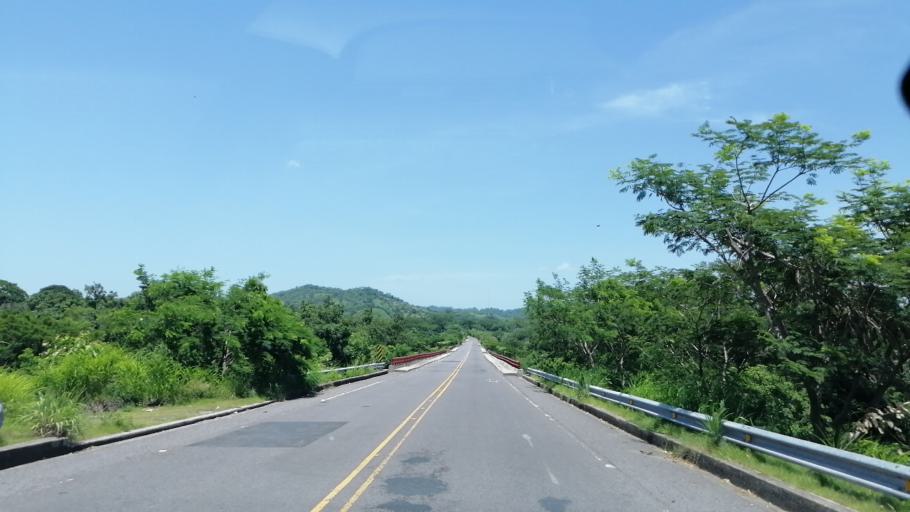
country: SV
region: Chalatenango
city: Chalatenango
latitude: 14.0393
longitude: -88.9675
